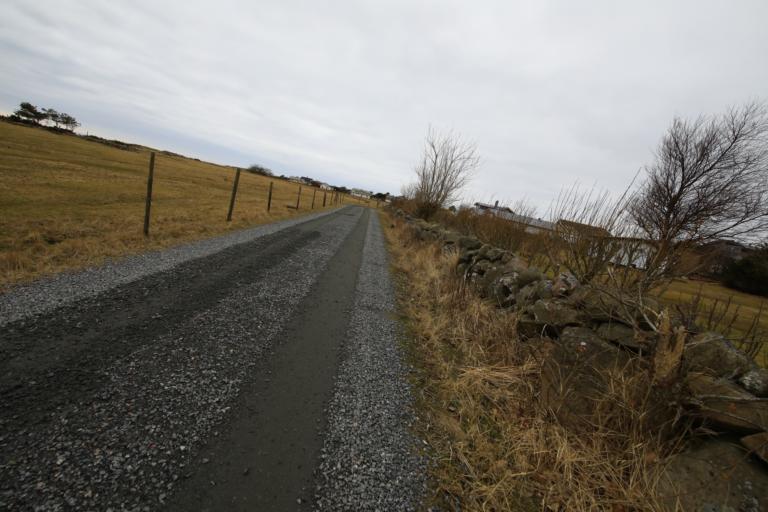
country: SE
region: Halland
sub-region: Varbergs Kommun
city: Traslovslage
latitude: 57.0694
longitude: 12.2659
